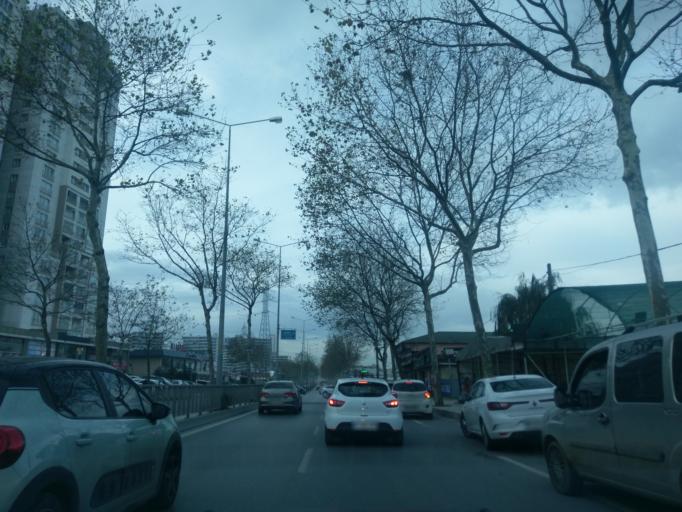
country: TR
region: Istanbul
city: Esenyurt
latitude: 41.0657
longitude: 28.6712
